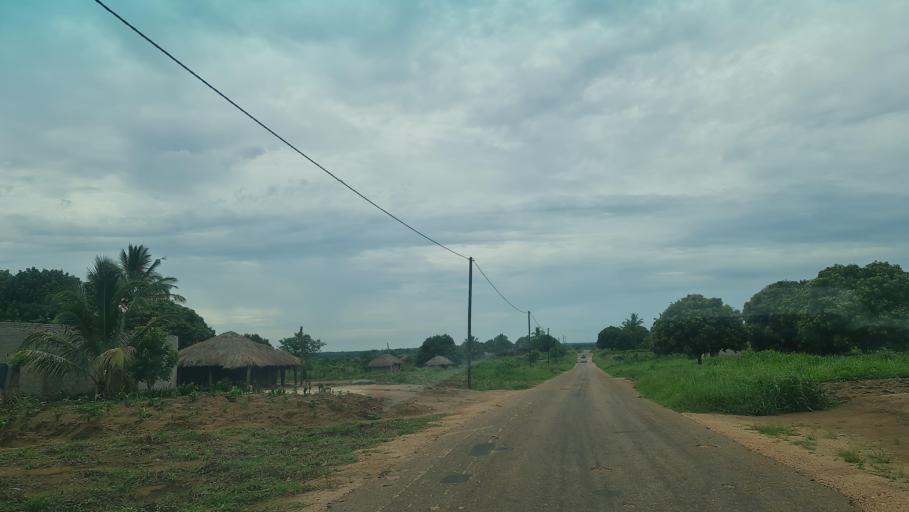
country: MW
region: Southern Region
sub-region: Nsanje District
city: Nsanje
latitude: -17.6755
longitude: 35.7202
